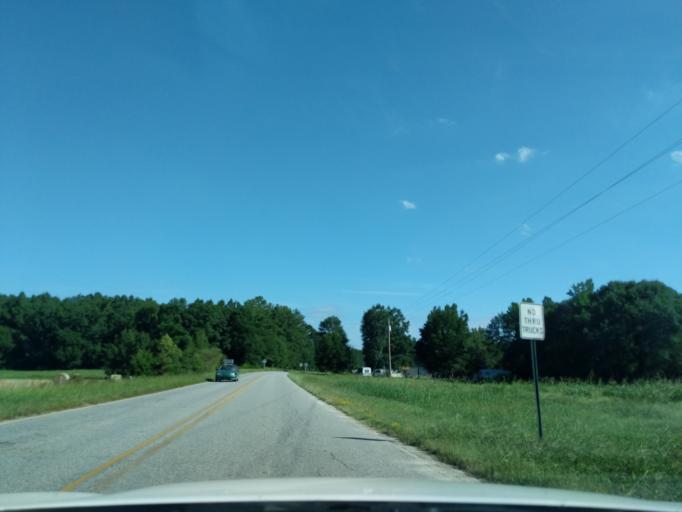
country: US
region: Georgia
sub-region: Oglethorpe County
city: Lexington
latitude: 33.9470
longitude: -83.0643
